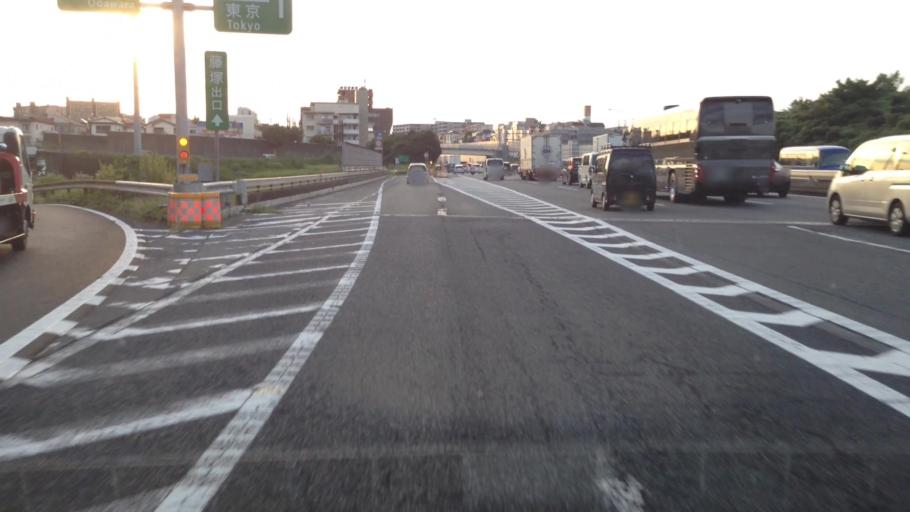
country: JP
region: Kanagawa
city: Yokohama
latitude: 35.4499
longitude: 139.5703
